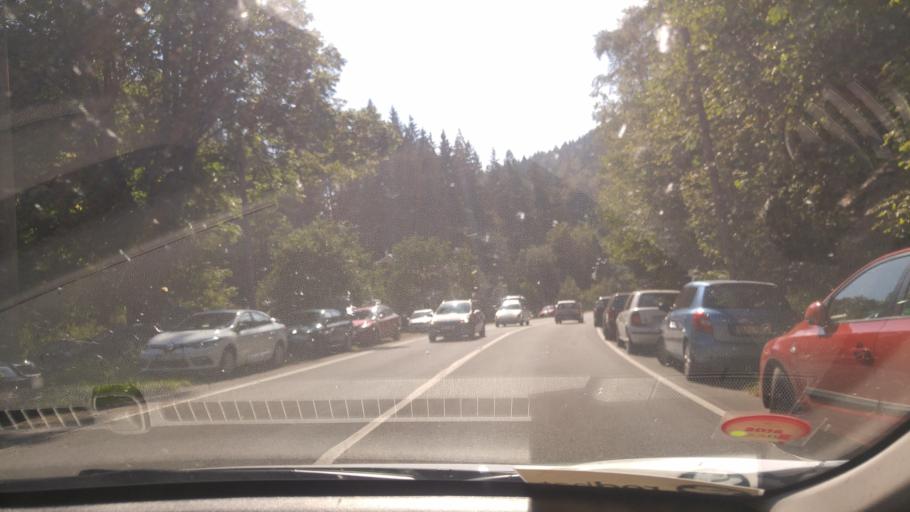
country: CZ
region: Olomoucky
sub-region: Okres Sumperk
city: Stare Mesto
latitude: 50.1453
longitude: 17.0139
